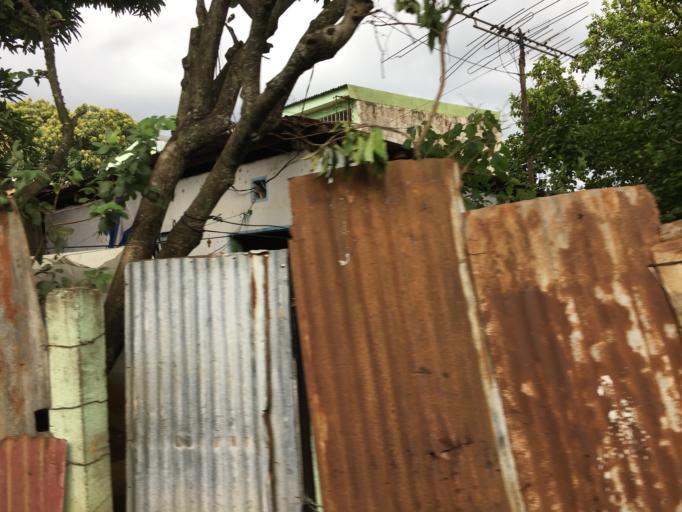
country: NI
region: Masaya
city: Masaya
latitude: 11.9837
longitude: -86.0933
